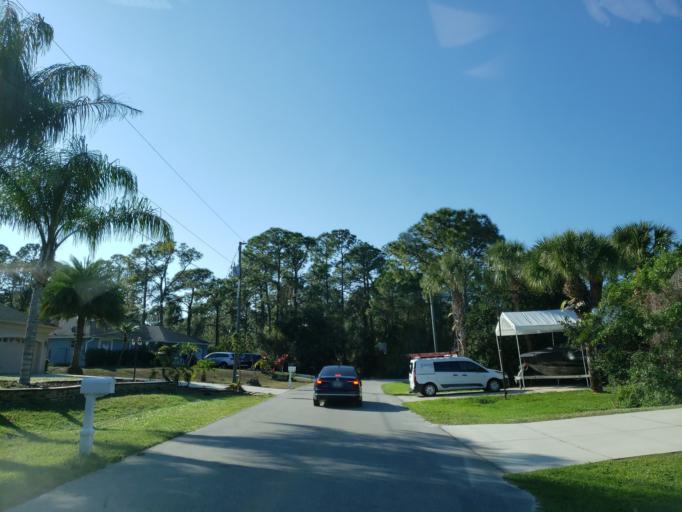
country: US
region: Florida
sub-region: Sarasota County
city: North Port
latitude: 27.0789
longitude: -82.1965
